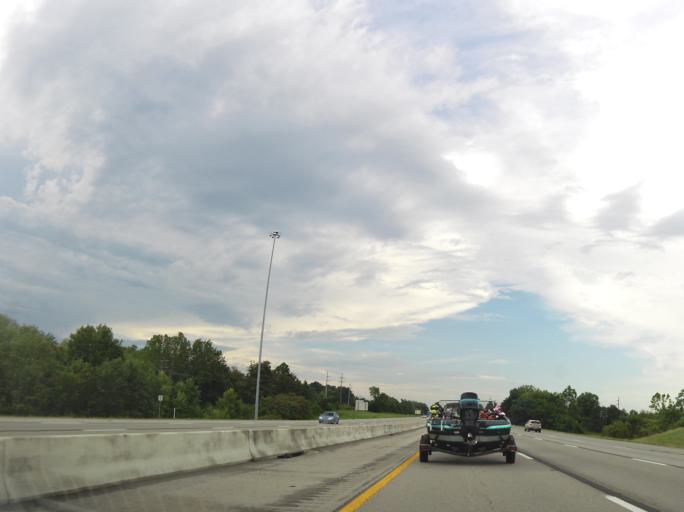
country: US
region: Kentucky
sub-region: Madison County
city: Berea
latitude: 37.5715
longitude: -84.3143
